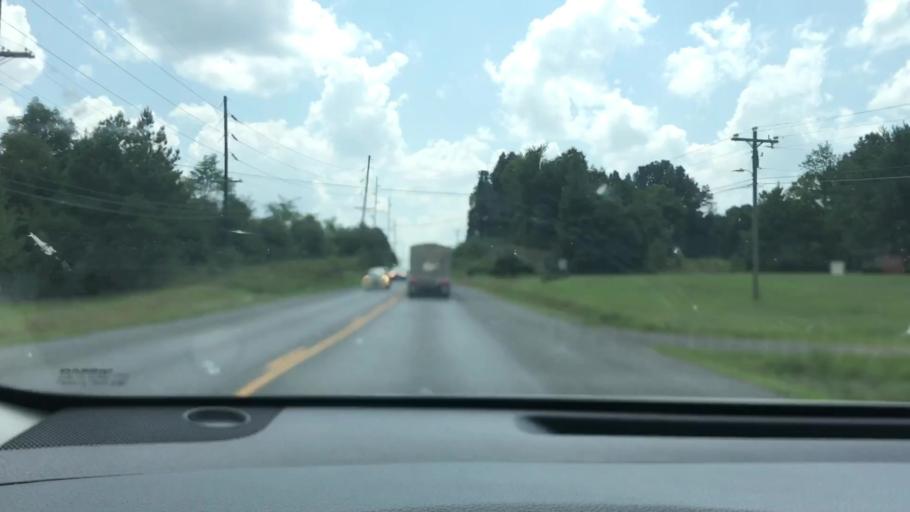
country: US
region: Kentucky
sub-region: Calloway County
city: Murray
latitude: 36.6257
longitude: -88.3020
